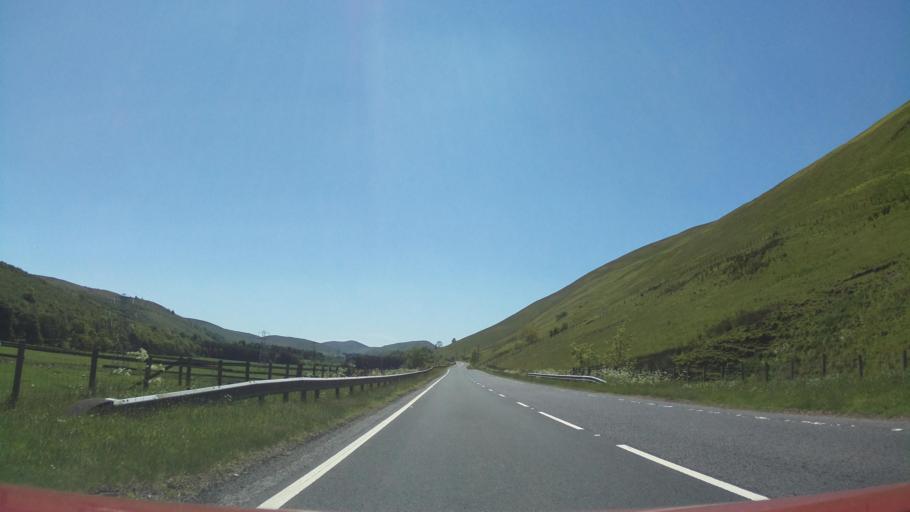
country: GB
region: Scotland
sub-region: Dumfries and Galloway
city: Langholm
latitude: 55.2437
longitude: -2.9695
